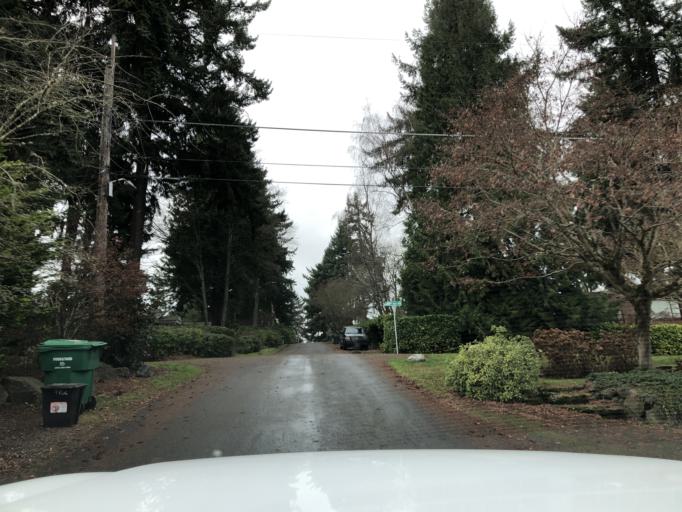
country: US
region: Washington
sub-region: King County
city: Inglewood-Finn Hill
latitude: 47.7011
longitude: -122.2749
